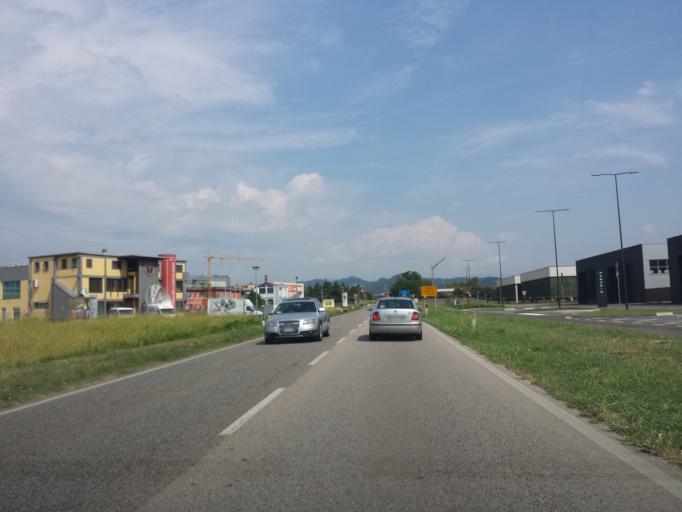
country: IT
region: Veneto
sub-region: Provincia di Vicenza
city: Trissino
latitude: 45.5532
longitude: 11.3845
